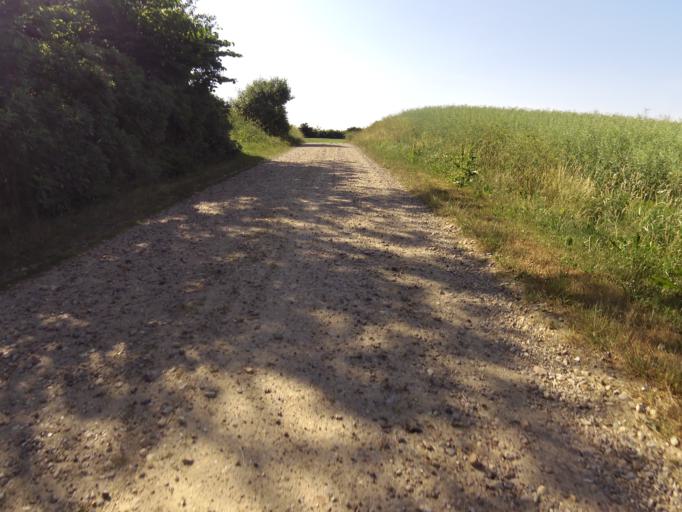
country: DK
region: Central Jutland
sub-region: Holstebro Kommune
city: Vinderup
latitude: 56.4448
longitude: 8.8239
